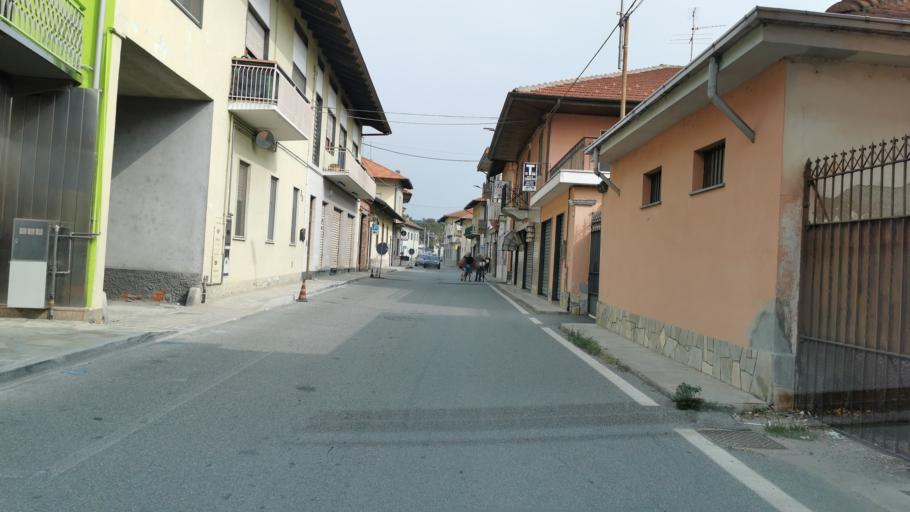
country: IT
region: Piedmont
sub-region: Provincia di Torino
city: Tonengo-Casale
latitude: 45.2868
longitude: 7.9374
